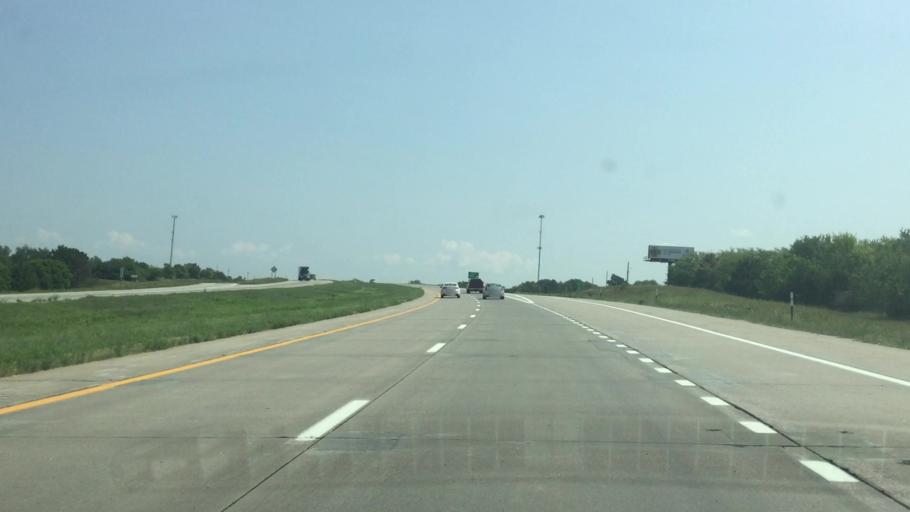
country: US
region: Kansas
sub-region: Osage County
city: Lyndon
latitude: 38.4875
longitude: -95.4768
